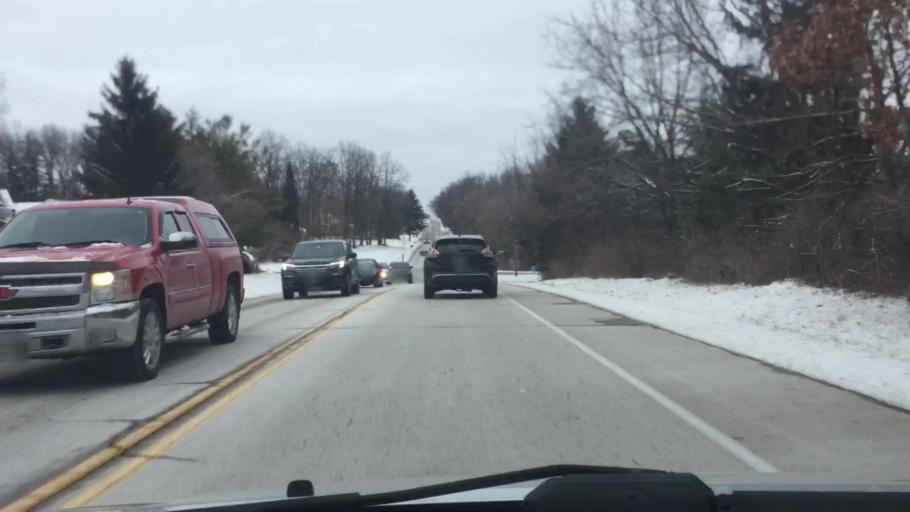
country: US
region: Wisconsin
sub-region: Waukesha County
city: Brookfield
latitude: 43.0692
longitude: -88.1060
